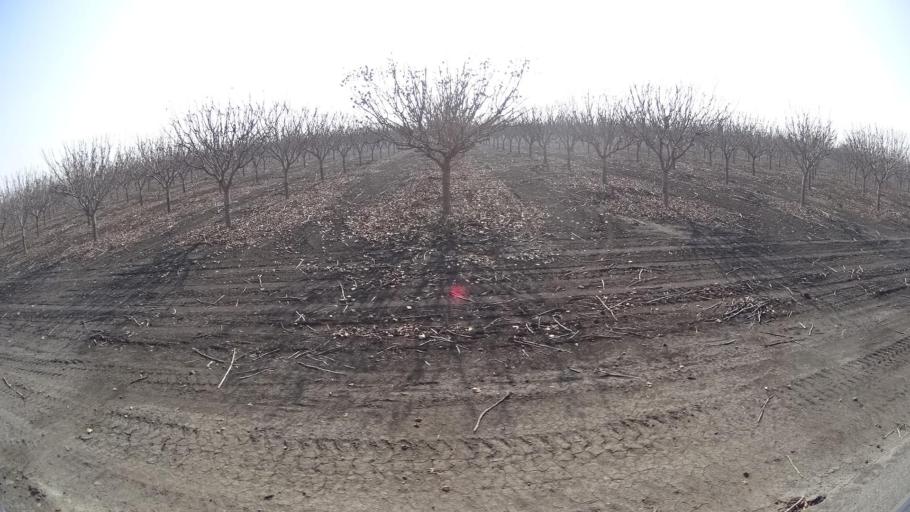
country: US
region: California
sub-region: Kern County
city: Buttonwillow
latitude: 35.3403
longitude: -119.4012
